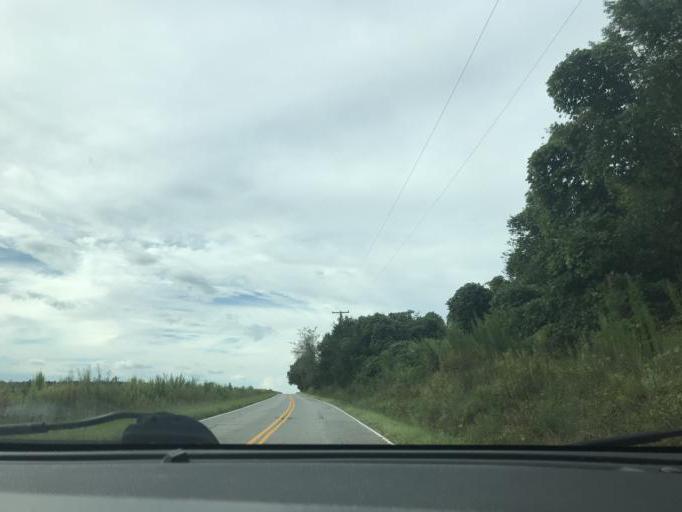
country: US
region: South Carolina
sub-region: Cherokee County
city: Gaffney
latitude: 35.1447
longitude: -81.6937
